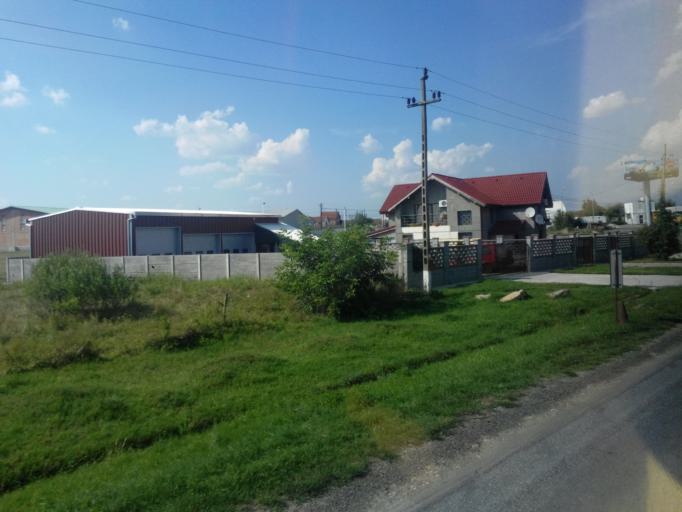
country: RO
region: Timis
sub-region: Comuna Giarmata
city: Giarmata
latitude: 45.8368
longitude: 21.2918
